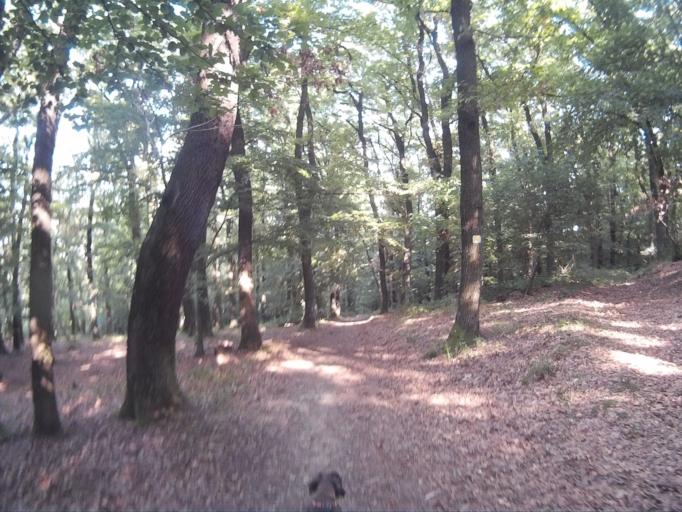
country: HU
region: Vas
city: Koszeg
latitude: 47.4000
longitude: 16.5199
